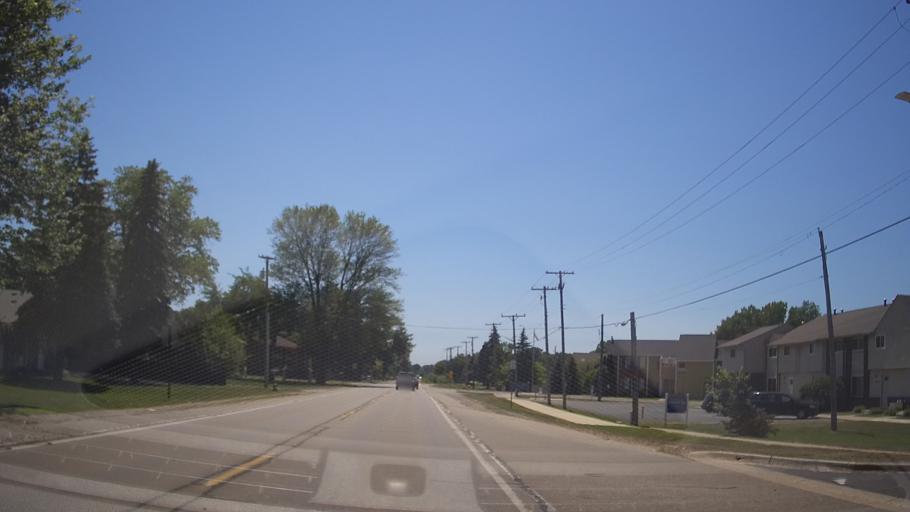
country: US
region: Michigan
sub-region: Macomb County
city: New Baltimore
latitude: 42.6729
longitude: -82.7520
